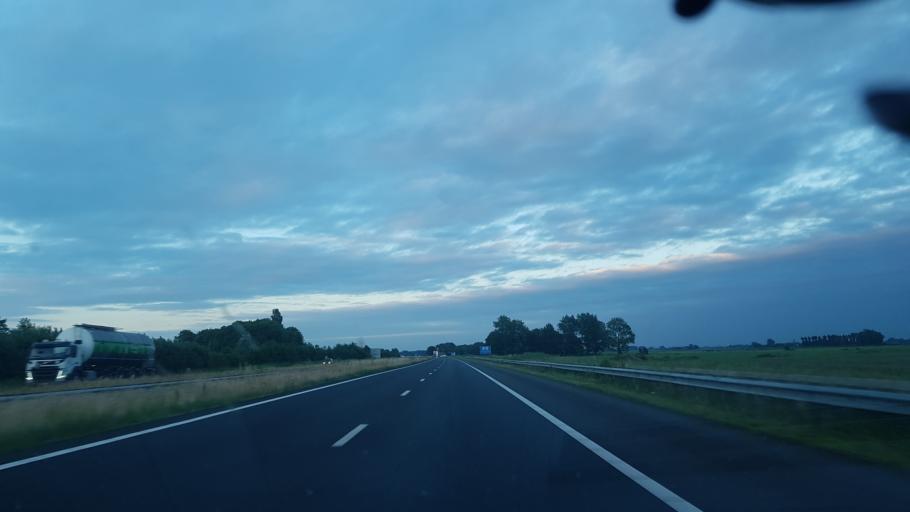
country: NL
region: Friesland
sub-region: Menameradiel
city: Menaam
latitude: 53.2025
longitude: 5.6683
